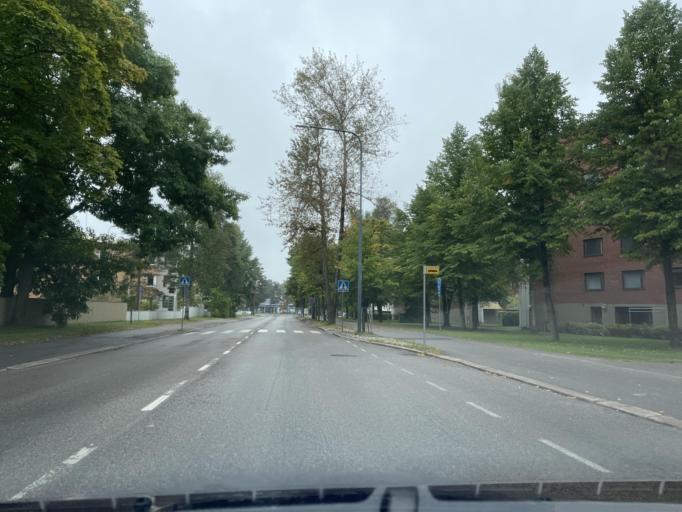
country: FI
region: Uusimaa
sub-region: Helsinki
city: Hyvinge
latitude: 60.6388
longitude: 24.8514
